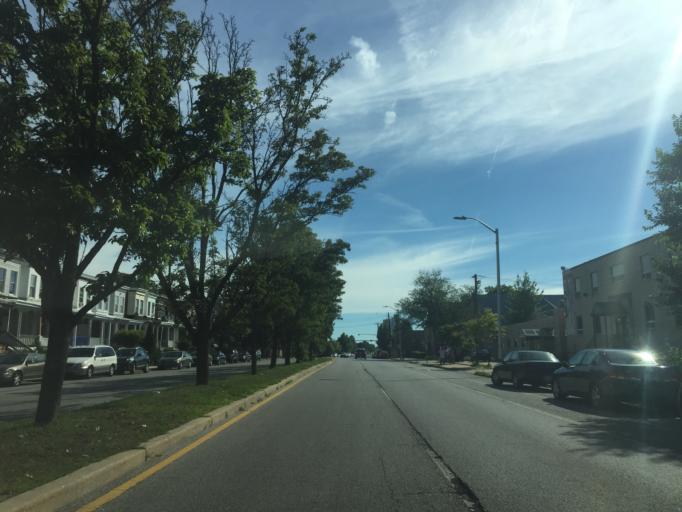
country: US
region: Maryland
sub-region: Baltimore County
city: Lochearn
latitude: 39.3478
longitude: -76.6777
